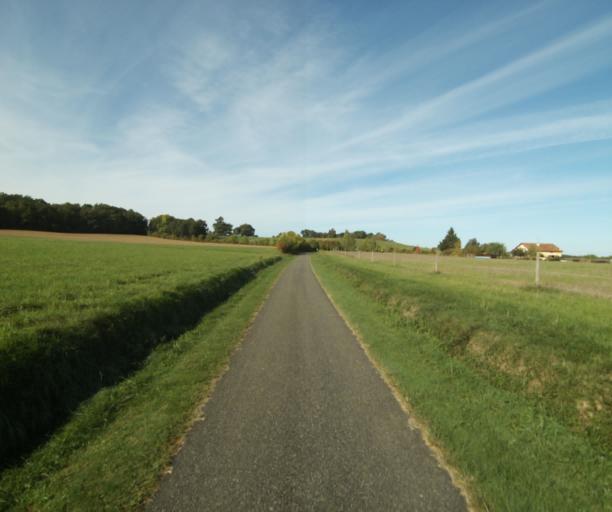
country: FR
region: Midi-Pyrenees
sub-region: Departement du Gers
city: Eauze
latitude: 43.9381
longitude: 0.1235
